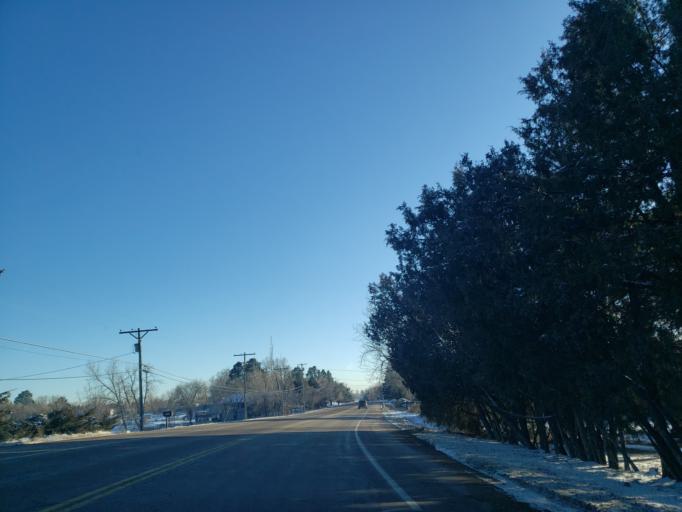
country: US
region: Colorado
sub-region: Larimer County
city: Fort Collins
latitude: 40.6271
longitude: -105.0709
